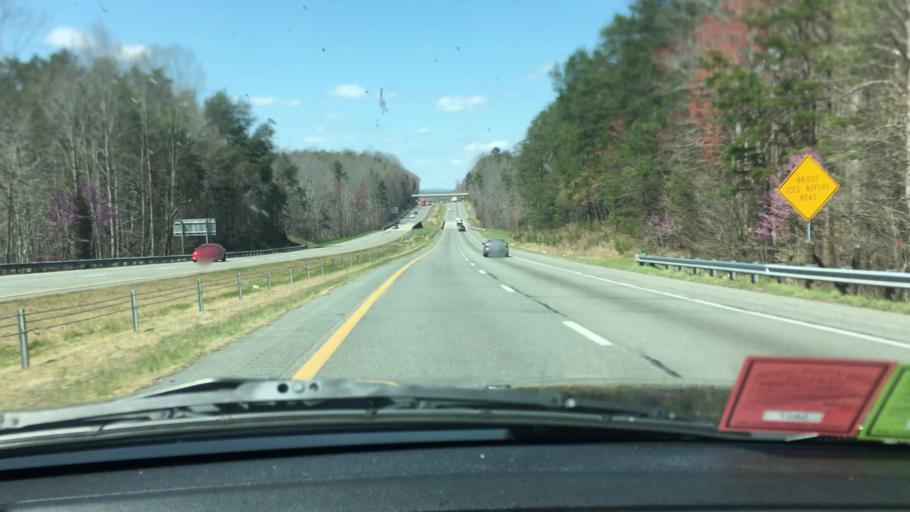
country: US
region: North Carolina
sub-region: Surry County
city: Pilot Mountain
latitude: 36.3823
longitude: -80.4890
